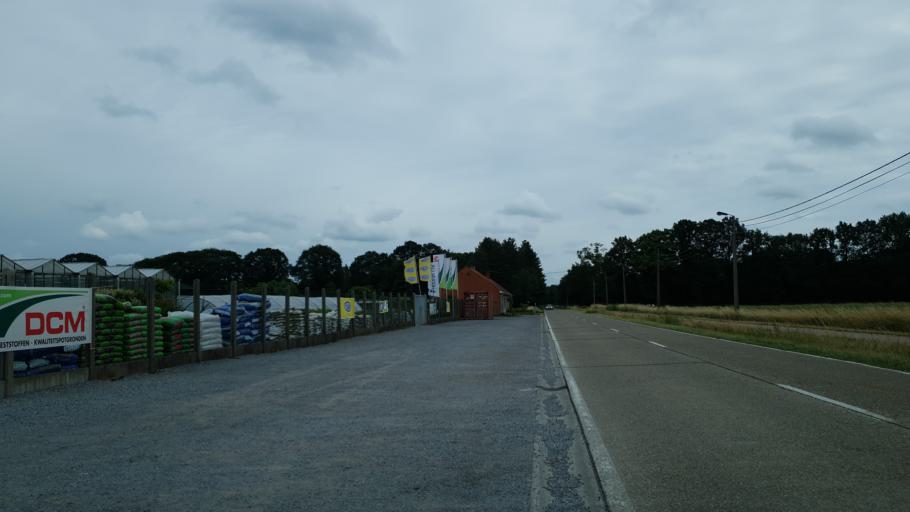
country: BE
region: Flanders
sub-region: Provincie Vlaams-Brabant
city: Scherpenheuvel-Zichem
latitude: 51.0497
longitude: 4.9481
